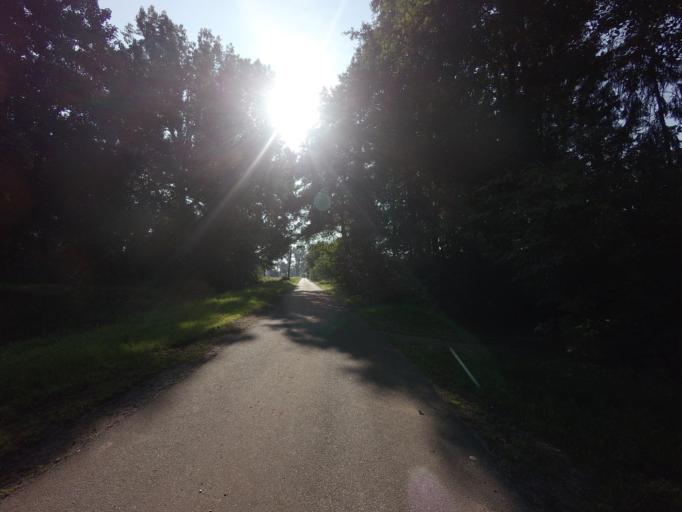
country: DE
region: Lower Saxony
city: Wielen
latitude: 52.5557
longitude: 6.7580
